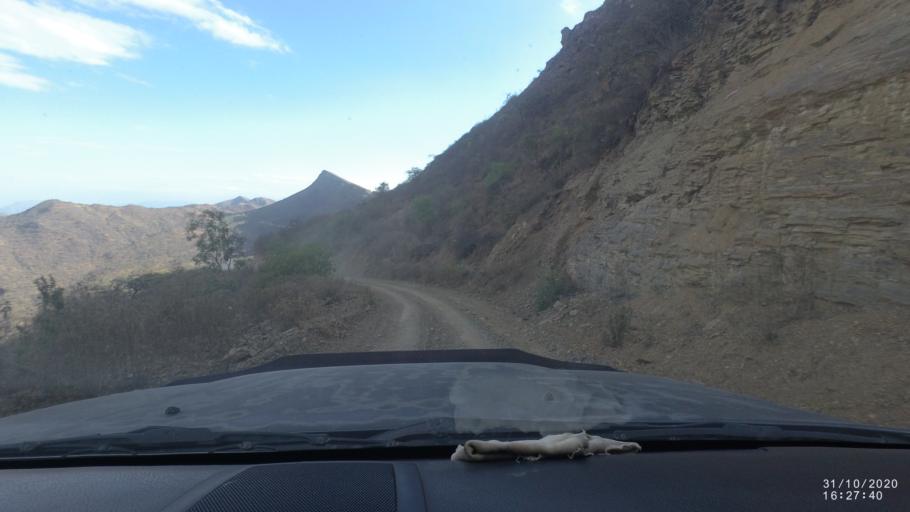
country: BO
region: Chuquisaca
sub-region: Provincia Zudanez
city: Mojocoya
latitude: -18.4078
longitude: -64.5863
